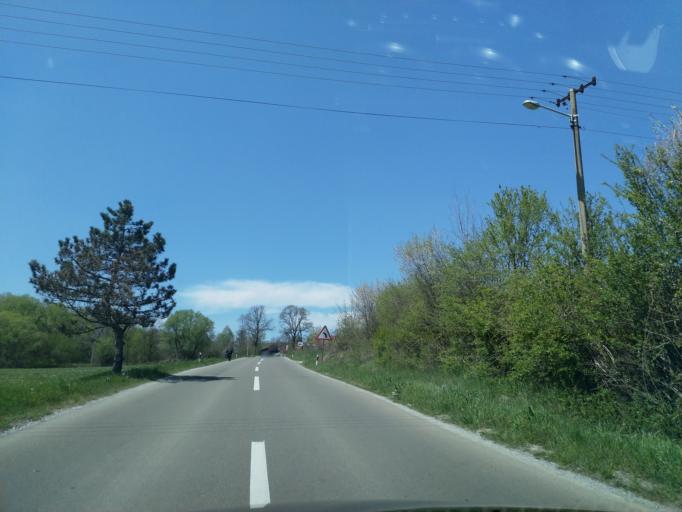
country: RS
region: Central Serbia
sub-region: Belgrade
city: Lazarevac
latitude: 44.3543
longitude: 20.3694
